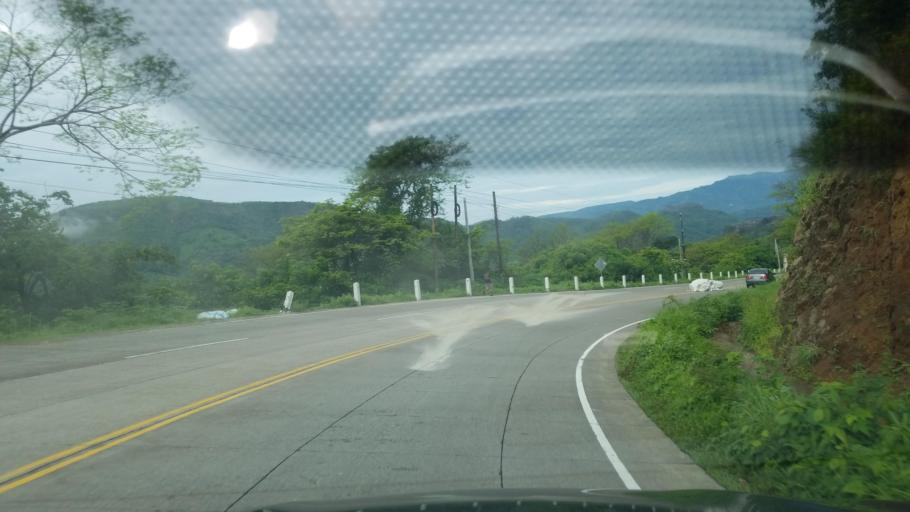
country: HN
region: Francisco Morazan
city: El Porvenir
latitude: 13.7004
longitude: -87.3157
